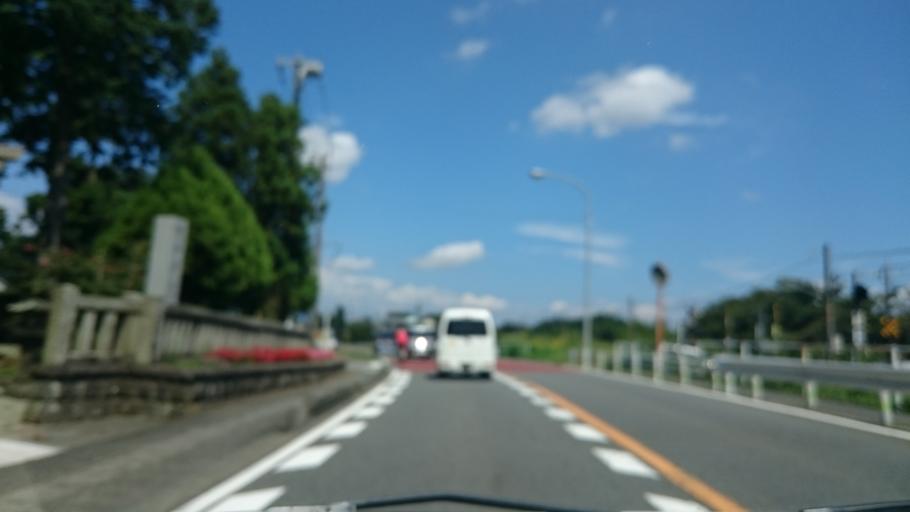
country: JP
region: Shizuoka
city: Gotemba
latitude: 35.2791
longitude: 138.9266
